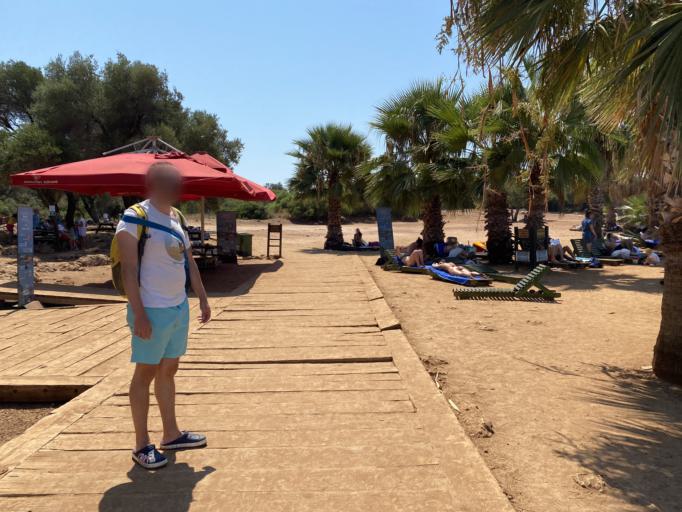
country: TR
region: Mugla
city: Yerkesik
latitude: 36.9930
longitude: 28.2037
